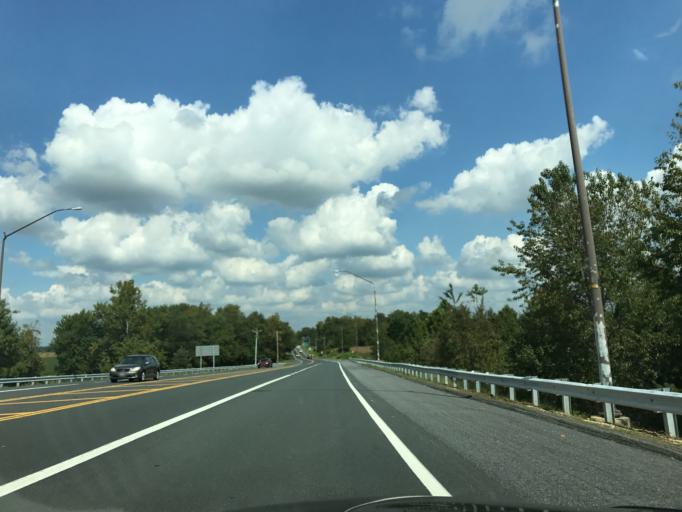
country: US
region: Maryland
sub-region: Queen Anne's County
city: Centreville
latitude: 39.0166
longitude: -76.0764
